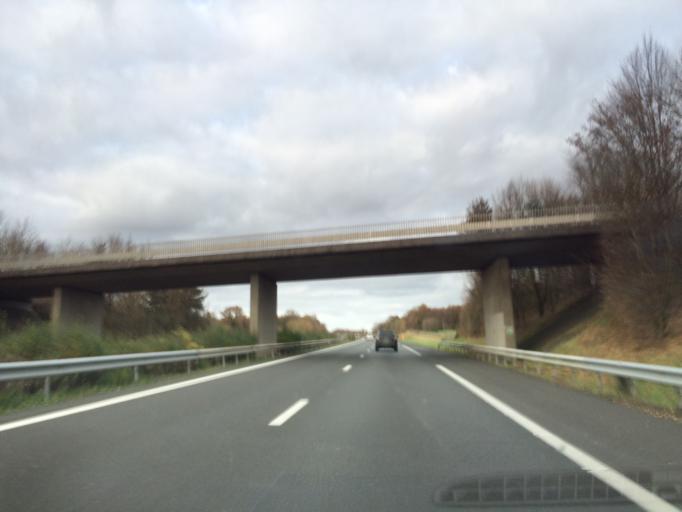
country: FR
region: Poitou-Charentes
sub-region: Departement des Deux-Sevres
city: Beauvoir-sur-Niort
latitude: 46.0777
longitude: -0.5312
